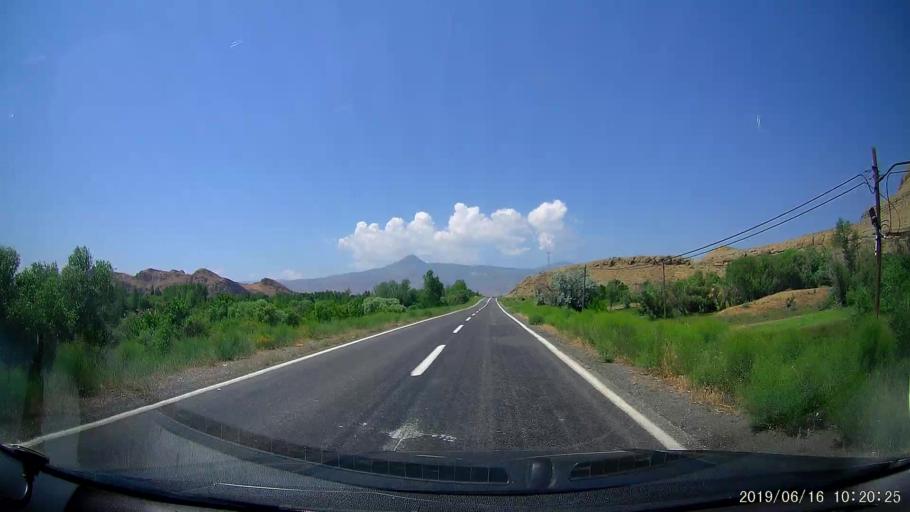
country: TR
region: Igdir
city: Tuzluca
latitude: 40.1480
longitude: 43.6480
